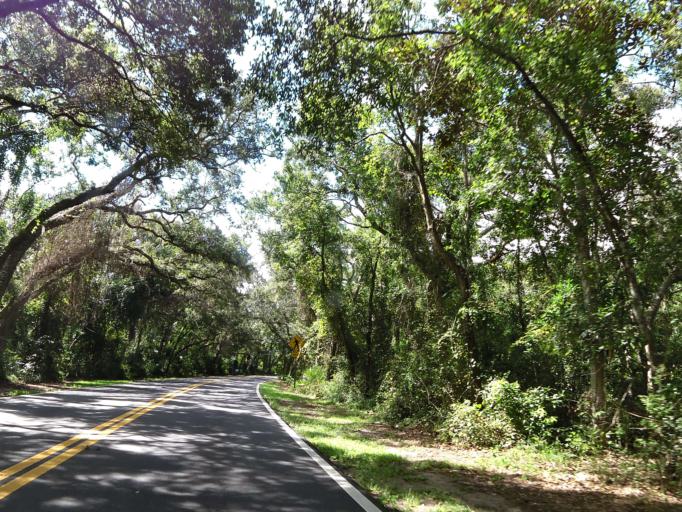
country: US
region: Florida
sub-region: Nassau County
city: Fernandina Beach
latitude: 30.5828
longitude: -81.4468
